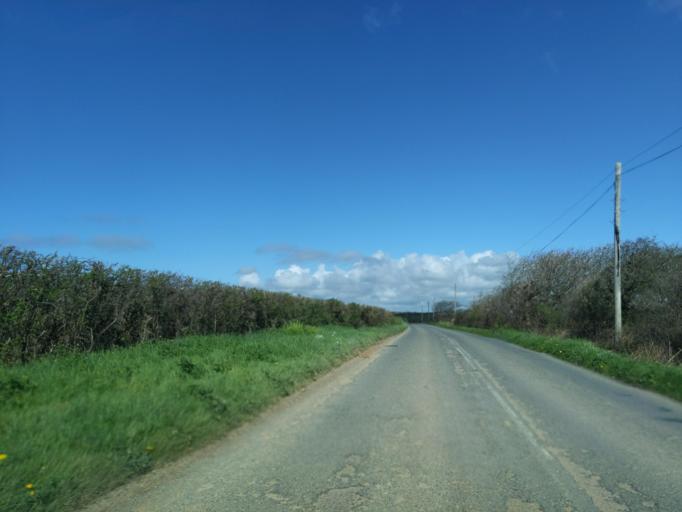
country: GB
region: England
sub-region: Cornwall
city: Tintagel
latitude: 50.5857
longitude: -4.7843
